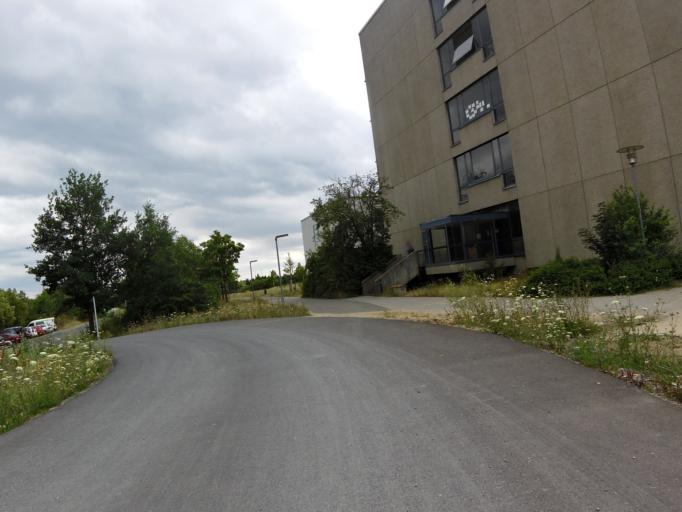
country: DE
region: Bavaria
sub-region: Regierungsbezirk Unterfranken
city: Wuerzburg
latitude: 49.7800
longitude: 9.9699
